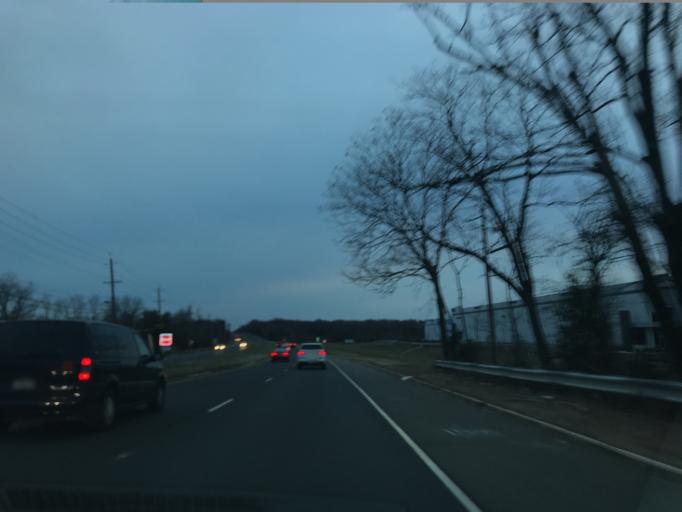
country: US
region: New Jersey
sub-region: Middlesex County
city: Dayton
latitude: 40.3727
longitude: -74.5005
